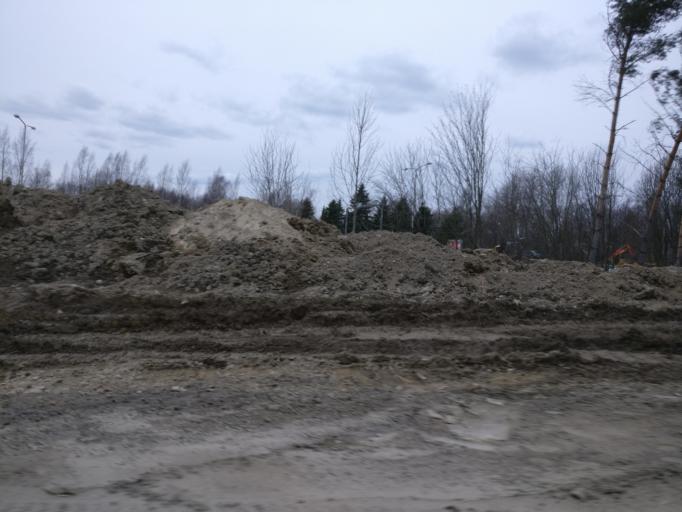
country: FI
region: Pirkanmaa
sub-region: Tampere
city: Tampere
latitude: 61.4845
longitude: 23.8286
